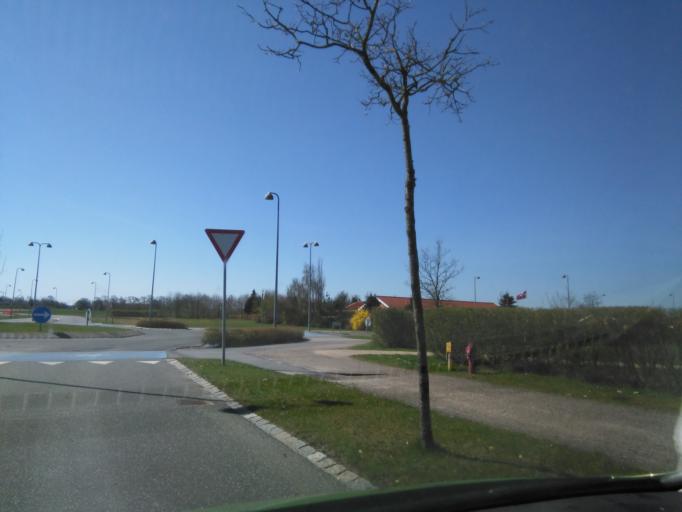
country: DK
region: South Denmark
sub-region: Billund Kommune
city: Billund
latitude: 55.7147
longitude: 9.1151
